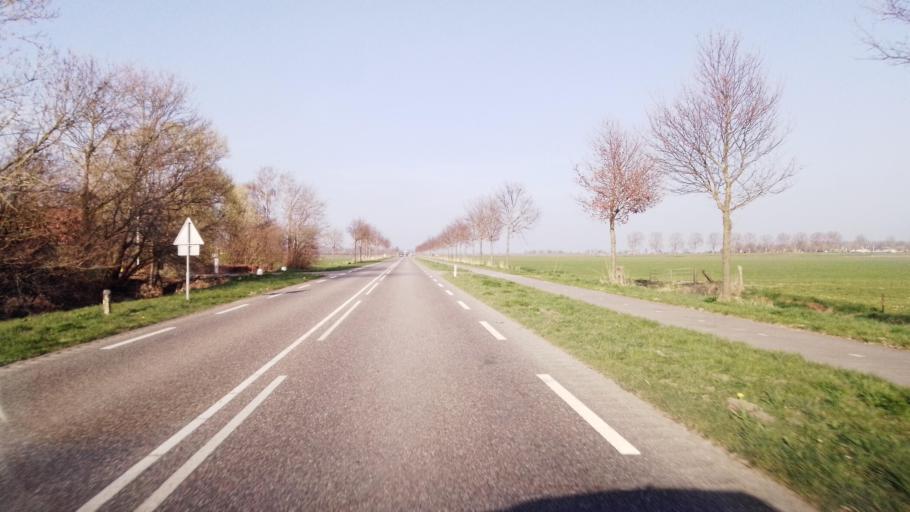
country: NL
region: Gelderland
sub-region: Gemeente Elburg
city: Elburg
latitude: 52.4571
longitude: 5.8001
